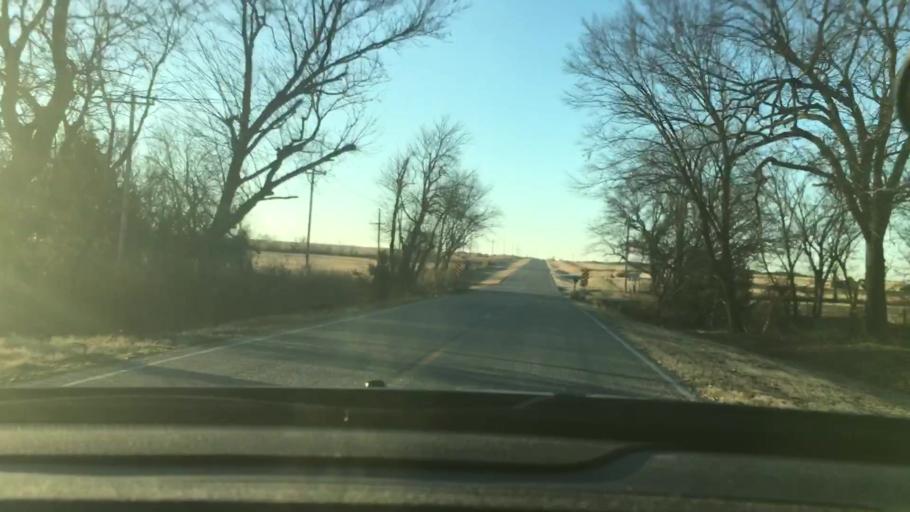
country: US
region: Oklahoma
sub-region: Murray County
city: Davis
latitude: 34.4832
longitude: -97.0906
